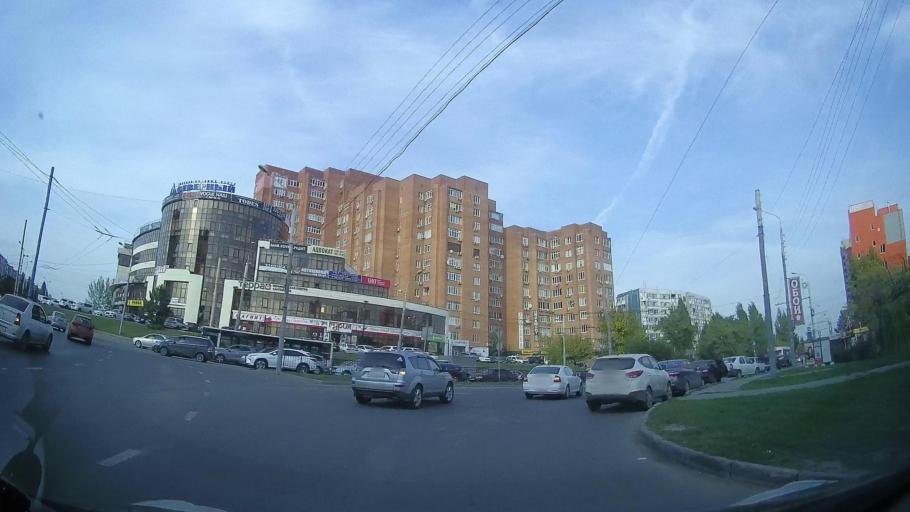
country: RU
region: Rostov
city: Severnyy
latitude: 47.2953
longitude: 39.7137
